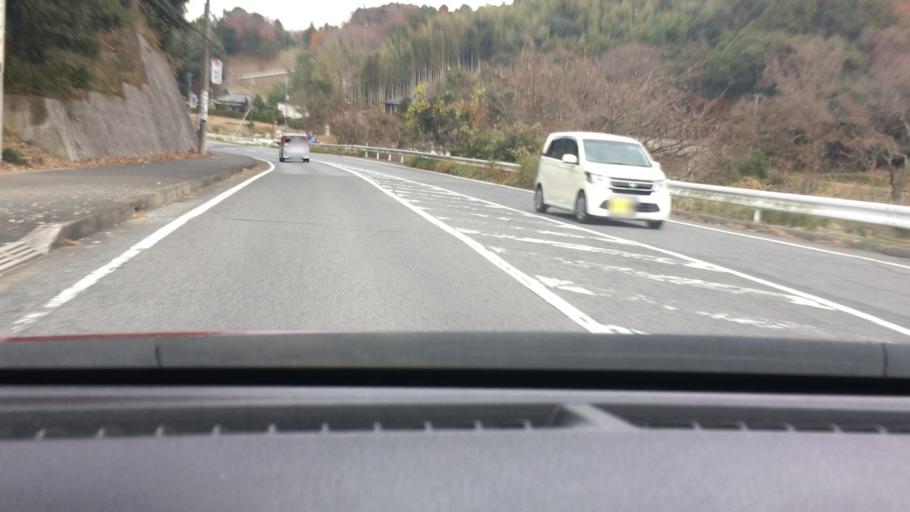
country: JP
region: Chiba
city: Ichihara
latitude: 35.4682
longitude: 140.0649
